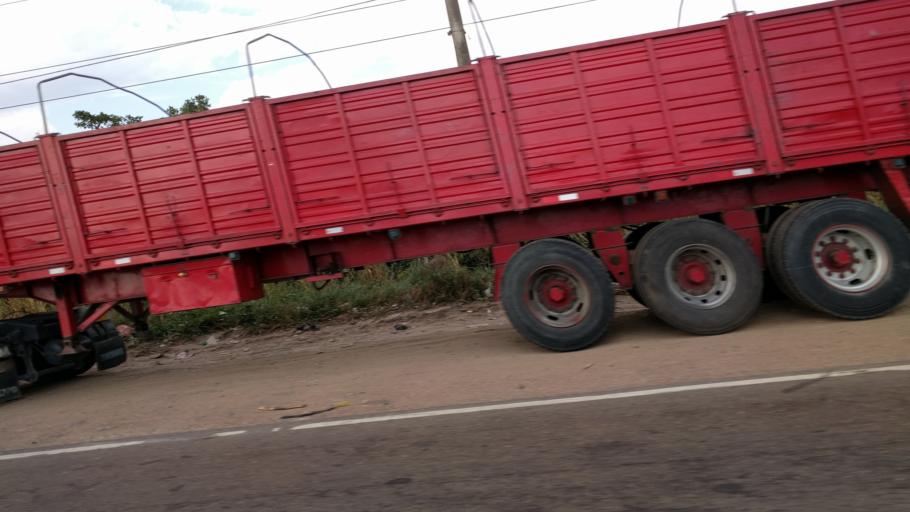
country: BO
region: Santa Cruz
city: Warnes
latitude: -17.5347
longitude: -63.1612
